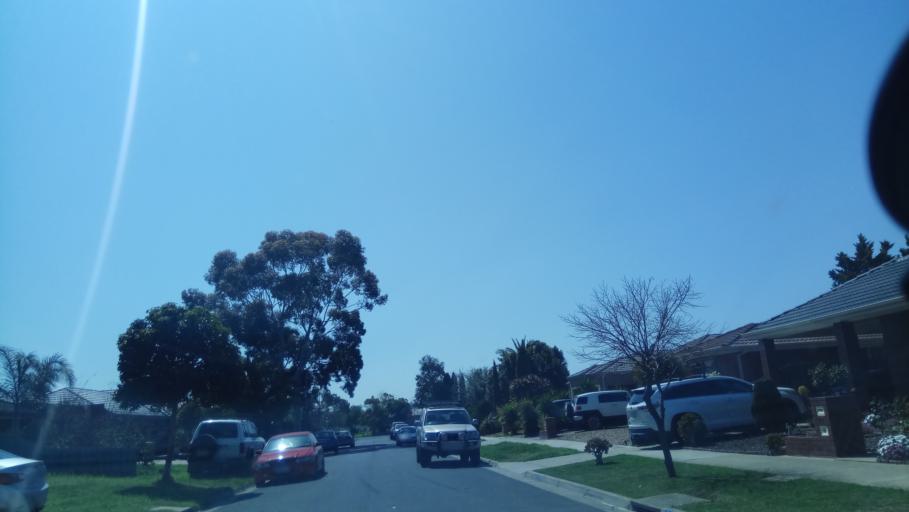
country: AU
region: Victoria
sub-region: Wyndham
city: Williams Landing
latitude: -37.8780
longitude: 144.7528
